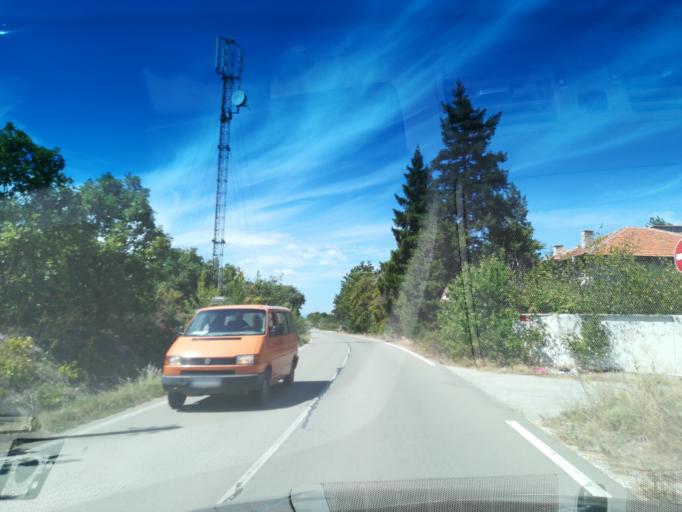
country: BG
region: Plovdiv
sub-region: Obshtina Suedinenie
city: Suedinenie
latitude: 42.3938
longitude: 24.5651
